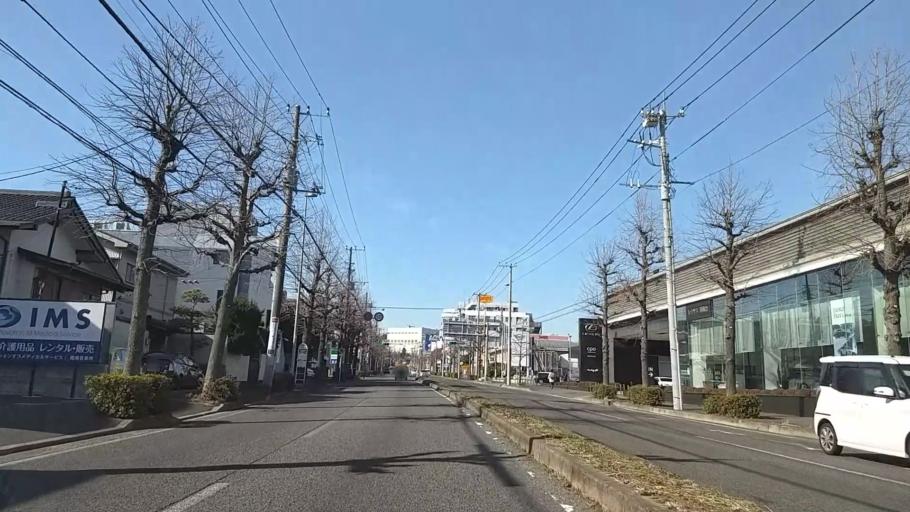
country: JP
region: Kanagawa
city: Kamakura
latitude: 35.3692
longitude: 139.5928
